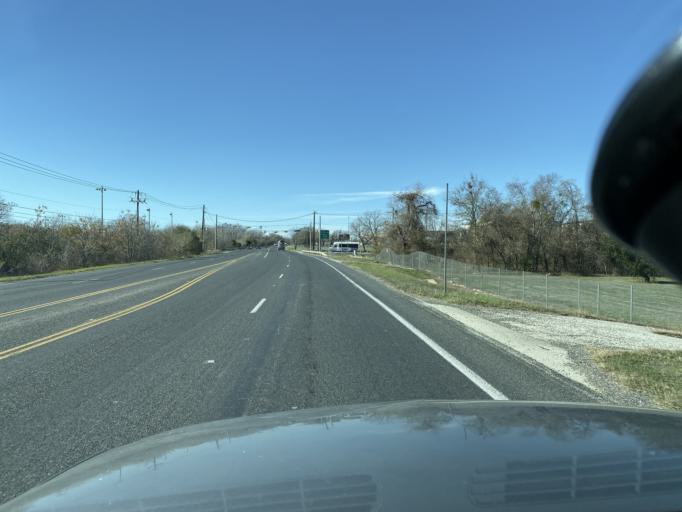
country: US
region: Texas
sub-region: Travis County
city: Garfield
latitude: 30.1728
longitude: -97.6691
